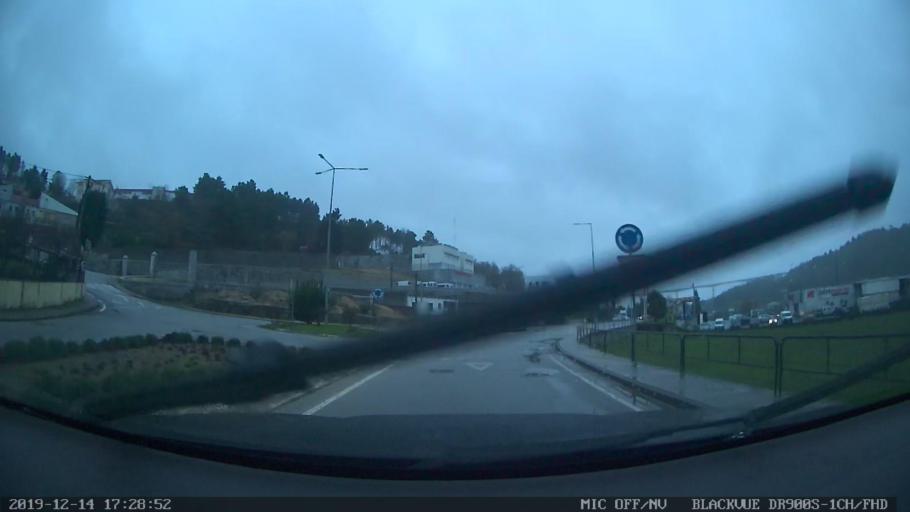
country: PT
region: Vila Real
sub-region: Vila Pouca de Aguiar
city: Vila Pouca de Aguiar
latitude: 41.4934
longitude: -7.6448
